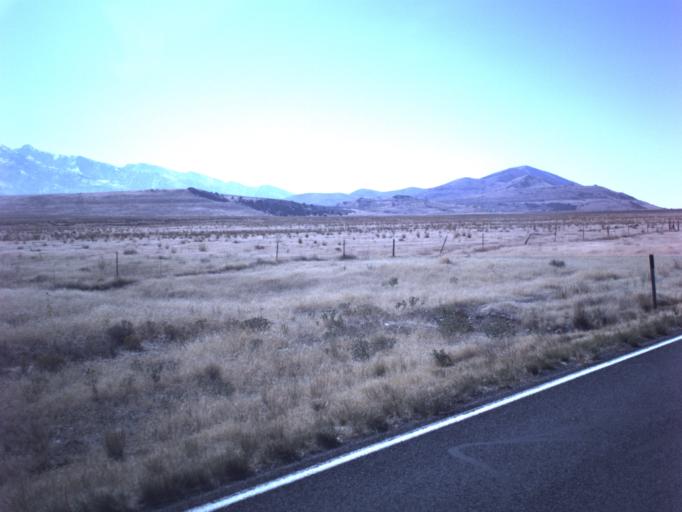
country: US
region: Utah
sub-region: Tooele County
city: Grantsville
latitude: 40.6060
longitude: -112.7094
